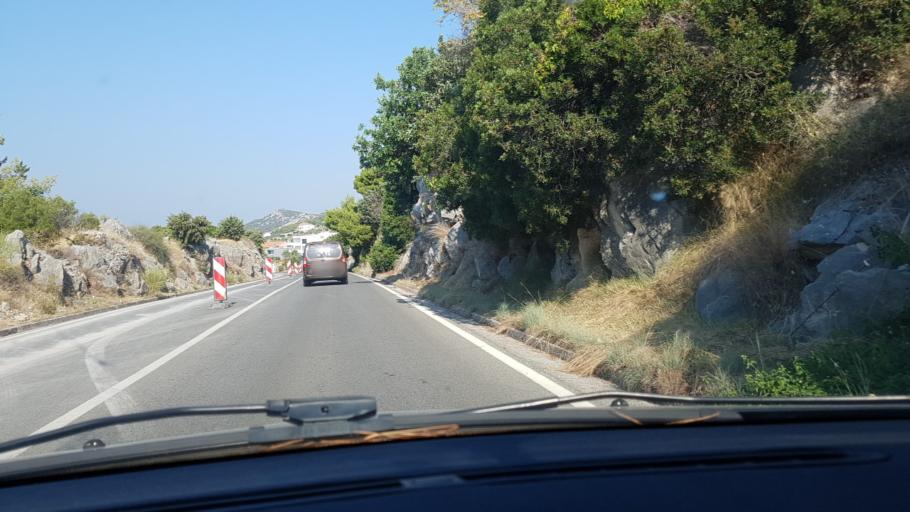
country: HR
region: Splitsko-Dalmatinska
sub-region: Grad Trogir
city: Trogir
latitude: 43.5145
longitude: 16.2019
